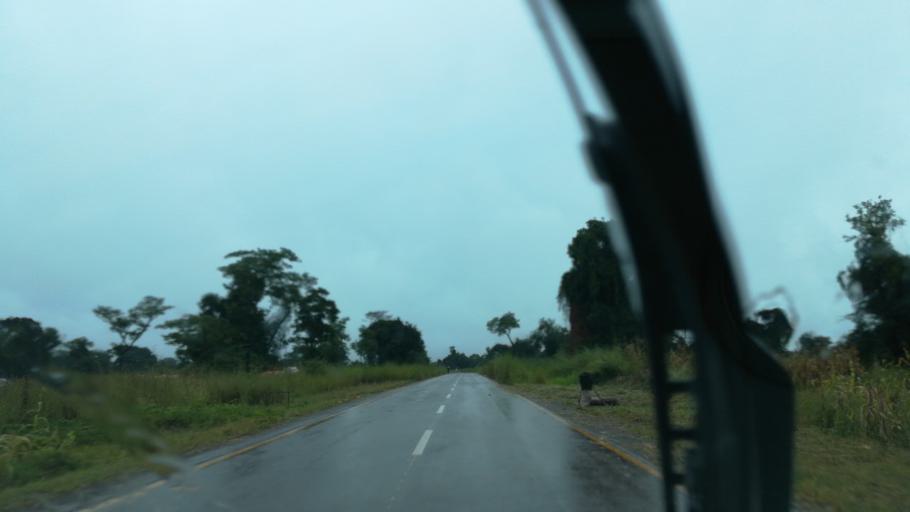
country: ZM
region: Luapula
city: Mwense
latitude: -10.8748
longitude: 28.2222
